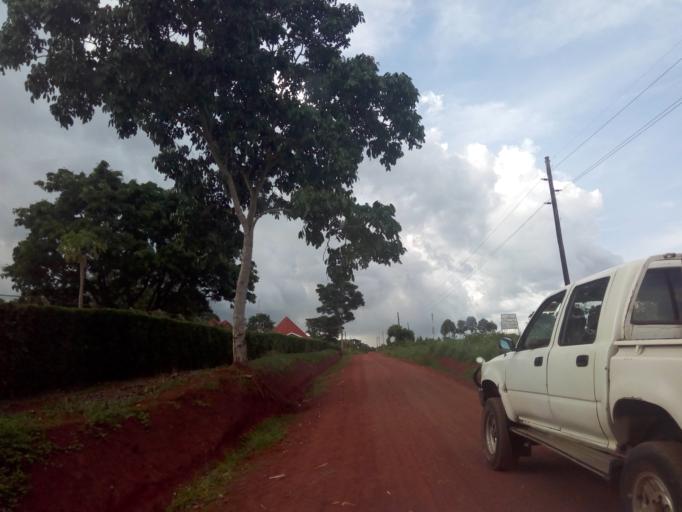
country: UG
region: Western Region
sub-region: Masindi District
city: Masindi
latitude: 1.6845
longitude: 31.7240
